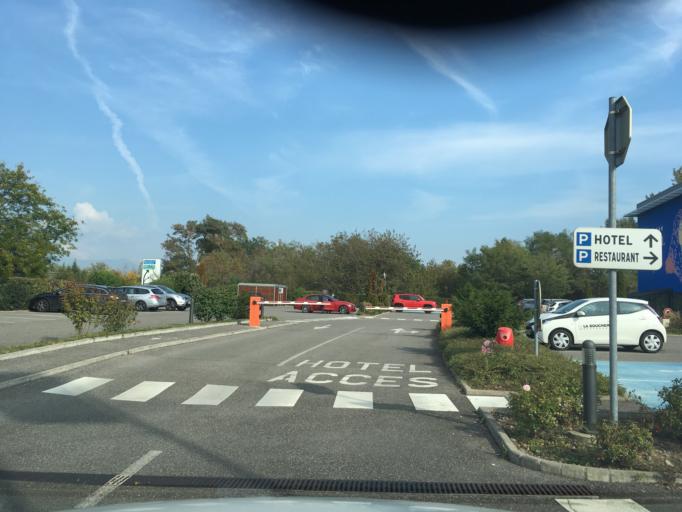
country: FR
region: Alsace
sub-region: Departement du Haut-Rhin
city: Houssen
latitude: 48.1124
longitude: 7.3648
